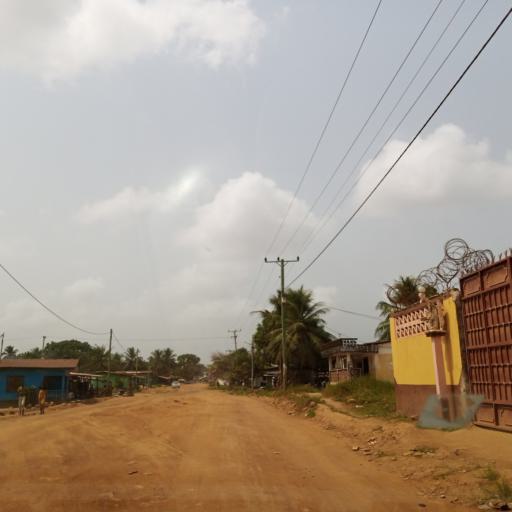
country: LR
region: Montserrado
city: Monrovia
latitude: 6.3497
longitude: -10.7291
